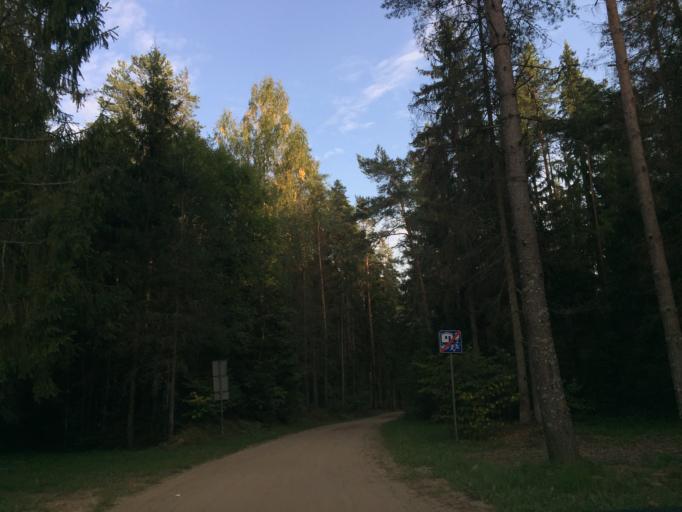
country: LV
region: Baldone
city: Baldone
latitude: 56.7686
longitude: 24.4039
